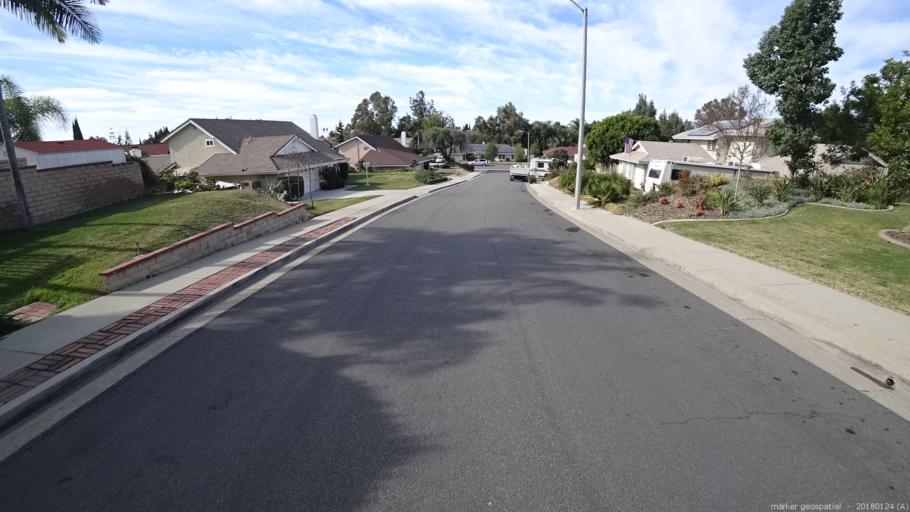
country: US
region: California
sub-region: Los Angeles County
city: Diamond Bar
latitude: 34.0157
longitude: -117.8127
